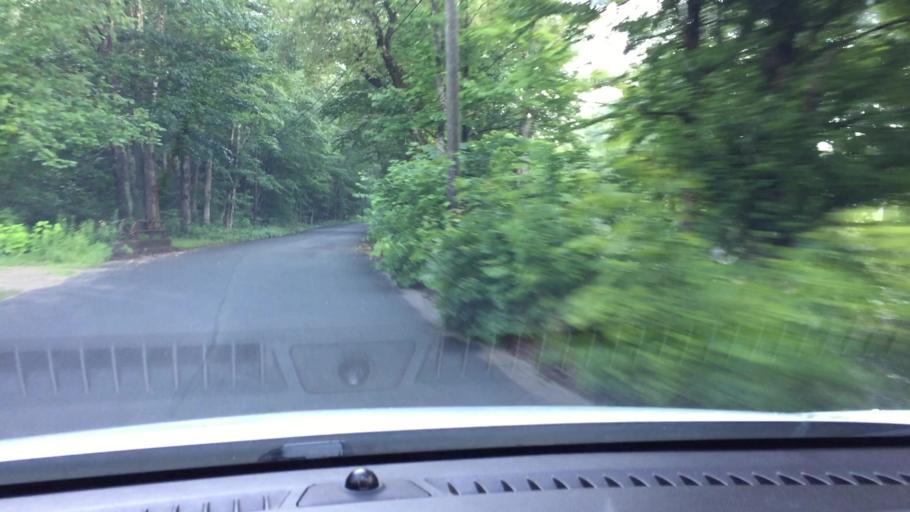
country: US
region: Massachusetts
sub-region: Hampshire County
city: Chesterfield
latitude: 42.3396
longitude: -72.9481
